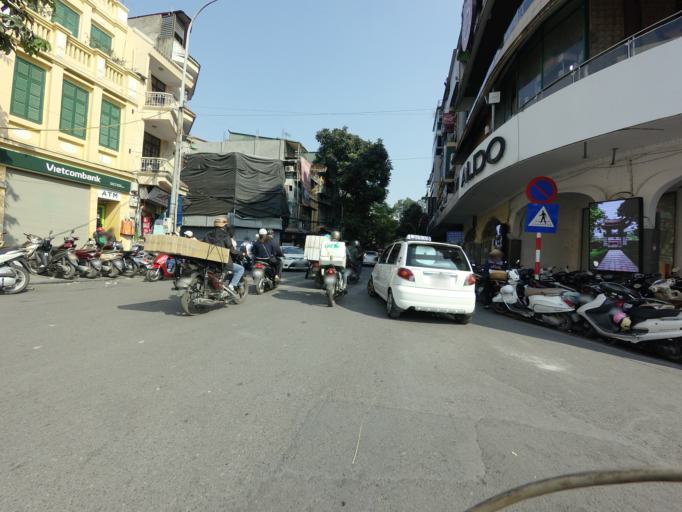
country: VN
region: Ha Noi
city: Hoan Kiem
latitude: 21.0323
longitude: 105.8517
